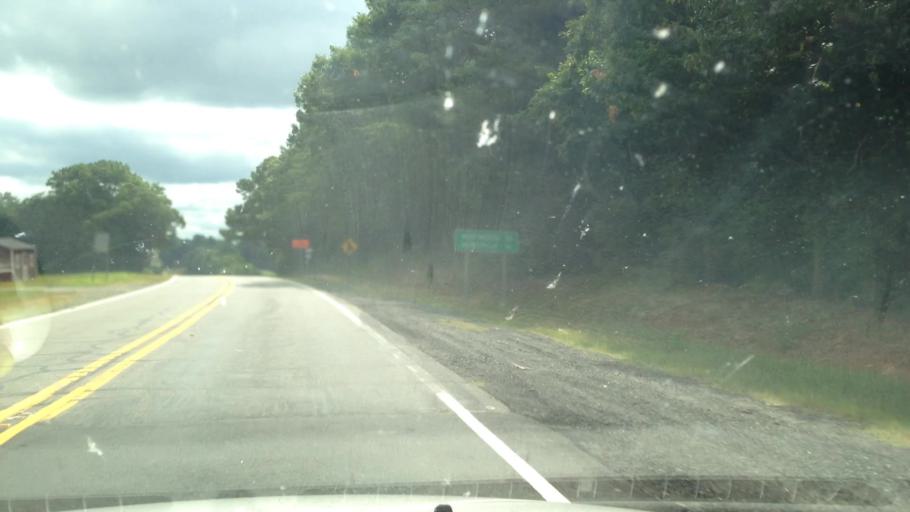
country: US
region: North Carolina
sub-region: Rockingham County
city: Madison
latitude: 36.3747
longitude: -79.9393
